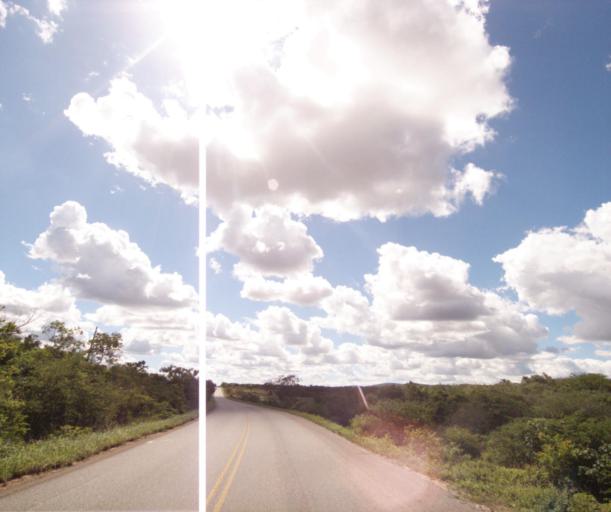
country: BR
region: Bahia
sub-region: Caetite
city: Caetite
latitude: -14.1676
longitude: -42.2390
